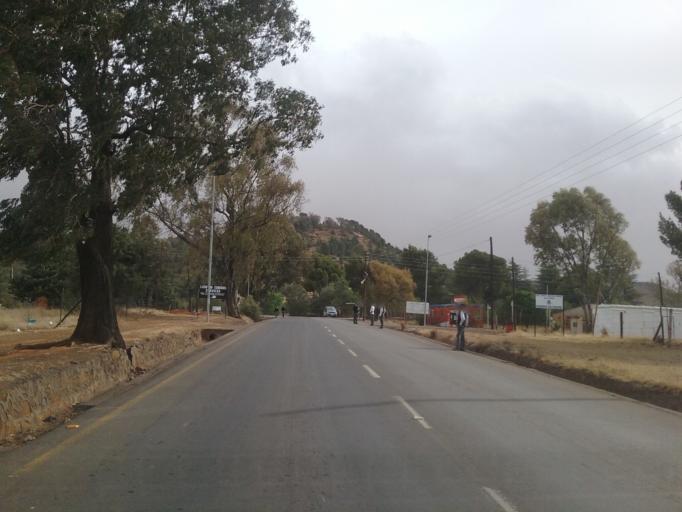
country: LS
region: Quthing
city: Quthing
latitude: -30.4052
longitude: 27.7083
